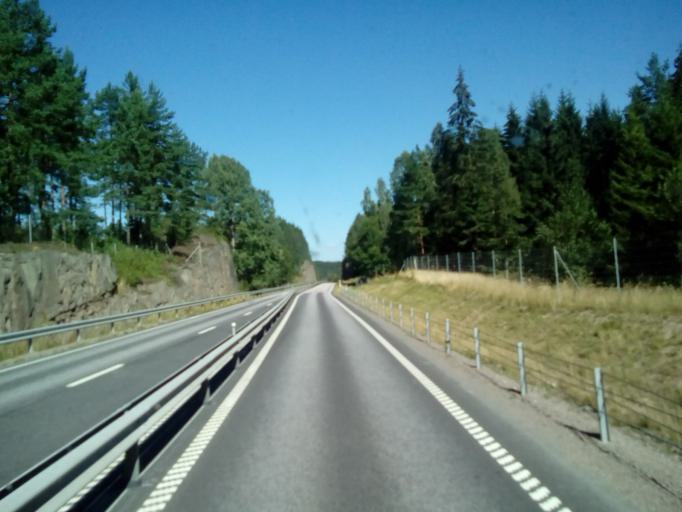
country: SE
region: OEstergoetland
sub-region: Kinda Kommun
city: Rimforsa
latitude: 58.0952
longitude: 15.6619
